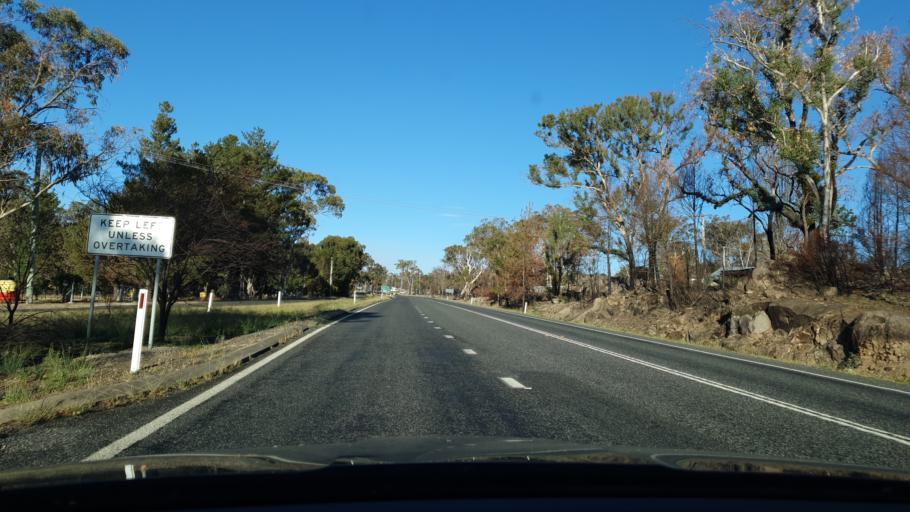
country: AU
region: Queensland
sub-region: Southern Downs
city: Stanthorpe
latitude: -28.6380
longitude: 151.9462
